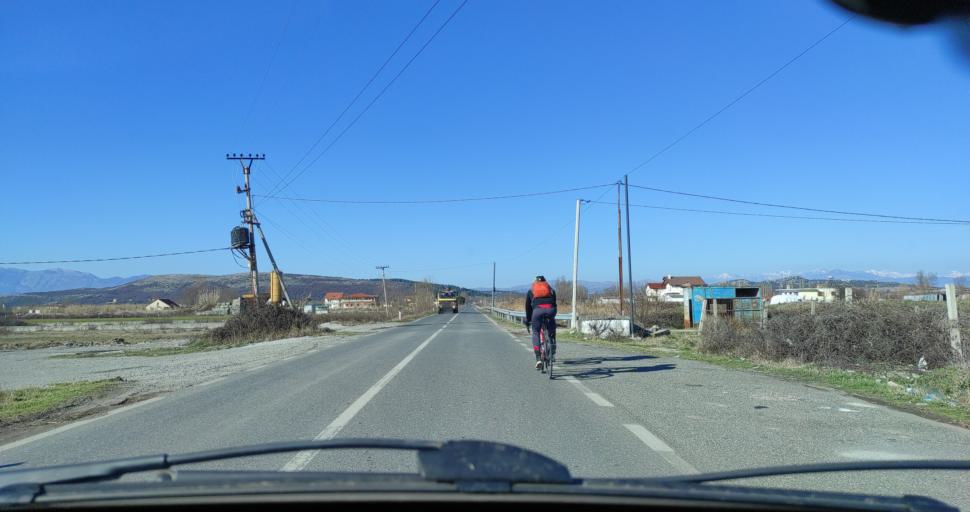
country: AL
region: Shkoder
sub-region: Rrethi i Shkodres
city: Velipoje
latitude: 41.8858
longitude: 19.4035
